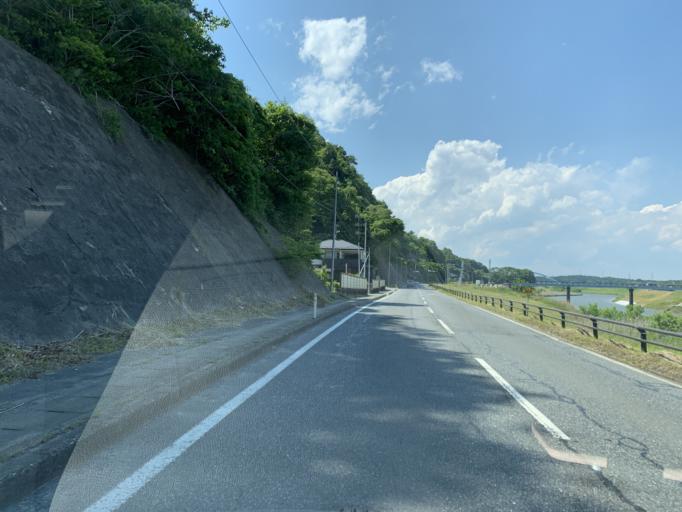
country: JP
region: Miyagi
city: Yamoto
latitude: 38.4044
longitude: 141.1484
